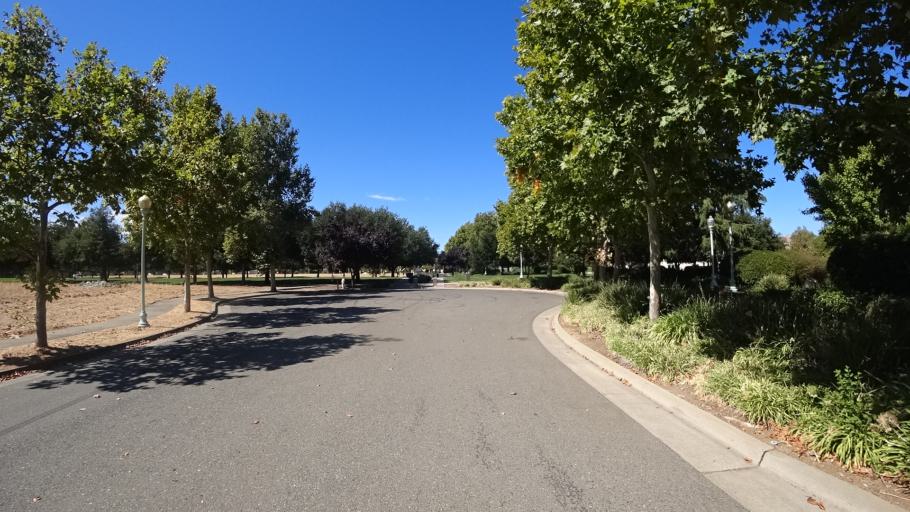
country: US
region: California
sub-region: Sacramento County
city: Laguna
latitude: 38.4243
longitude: -121.4694
